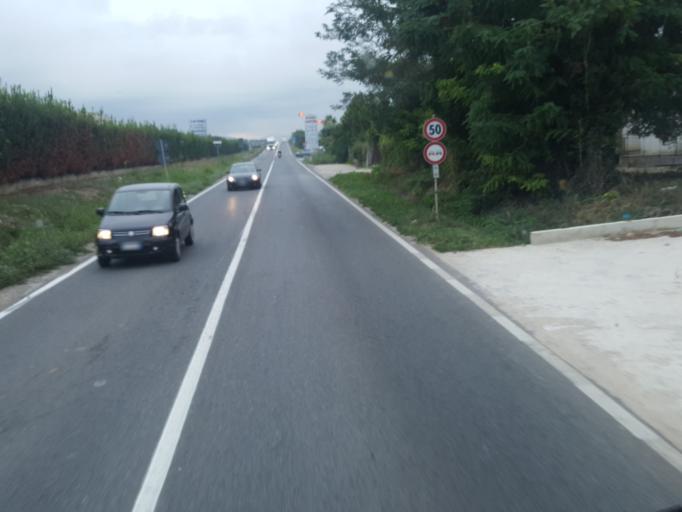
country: IT
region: Campania
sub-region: Provincia di Caserta
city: Pignataro Maggiore
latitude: 41.1647
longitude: 14.1634
